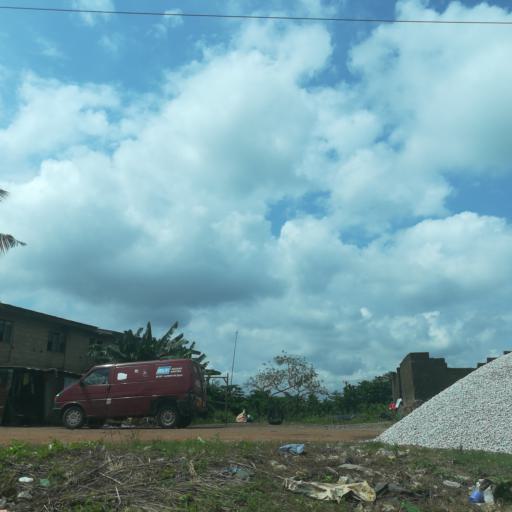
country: NG
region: Lagos
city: Ejirin
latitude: 6.6502
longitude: 3.7085
